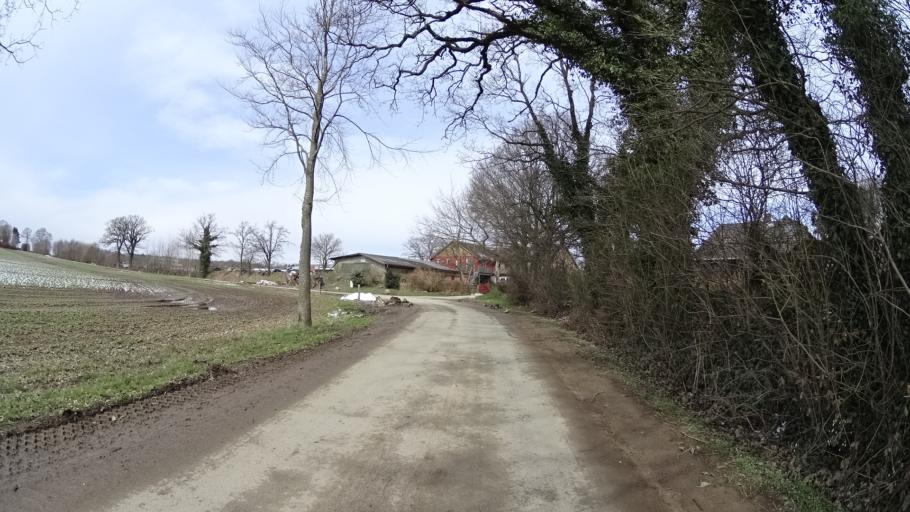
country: DE
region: Schleswig-Holstein
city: Rendswuhren
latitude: 54.0955
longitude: 10.1918
